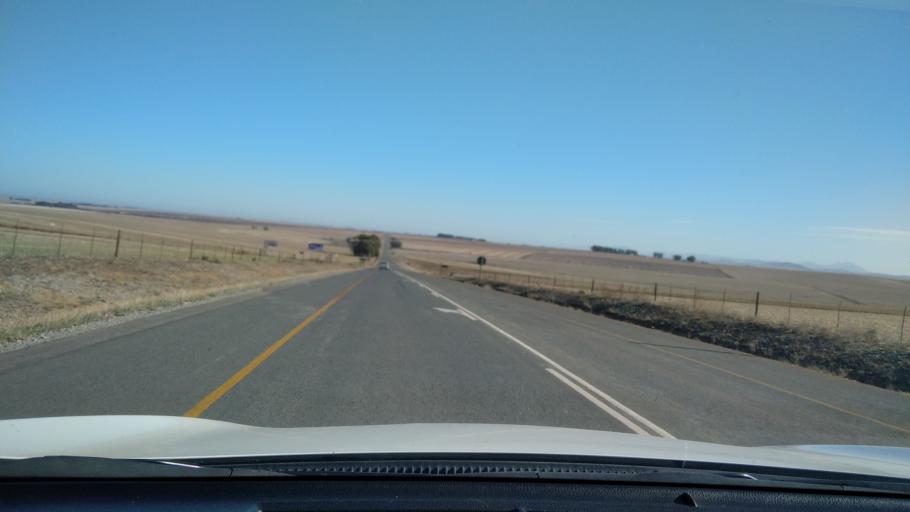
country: ZA
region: Western Cape
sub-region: West Coast District Municipality
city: Malmesbury
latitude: -33.3601
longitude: 18.6463
